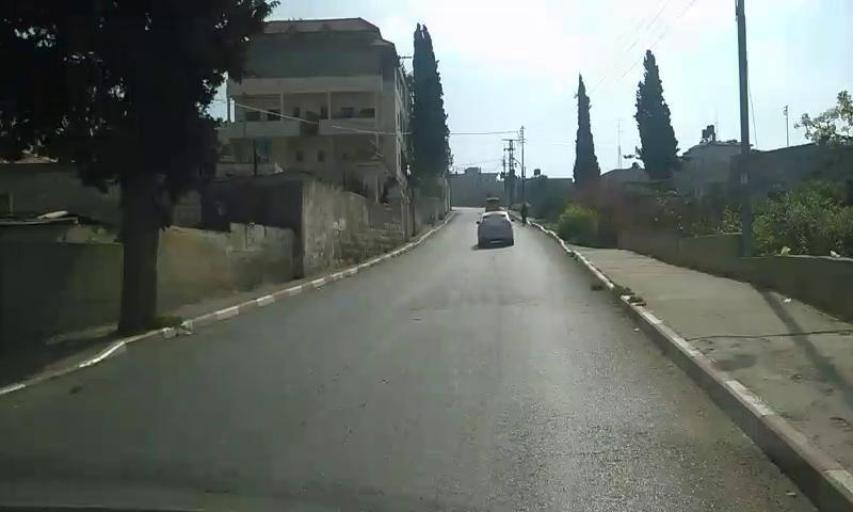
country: PS
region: West Bank
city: `Ayn Yabrud
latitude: 31.9543
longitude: 35.2485
